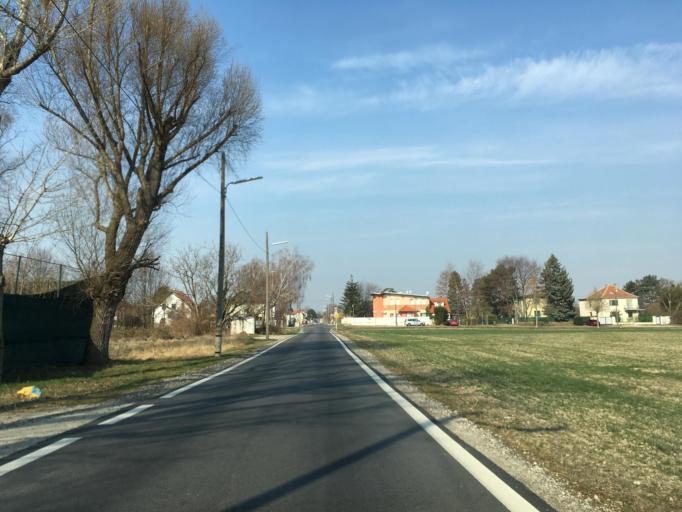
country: AT
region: Lower Austria
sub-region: Politischer Bezirk Ganserndorf
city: Gross-Enzersdorf
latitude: 48.2049
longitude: 16.4888
